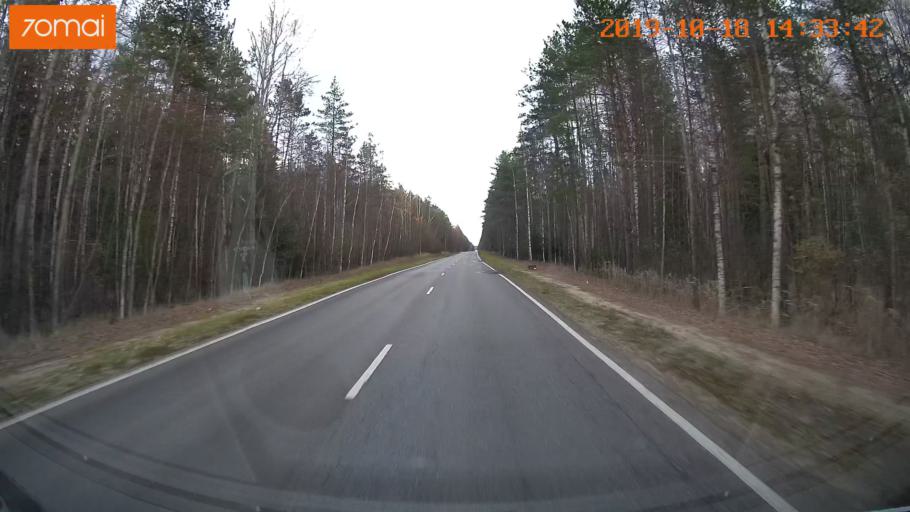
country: RU
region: Rjazan
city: Tuma
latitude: 55.2043
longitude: 40.6018
